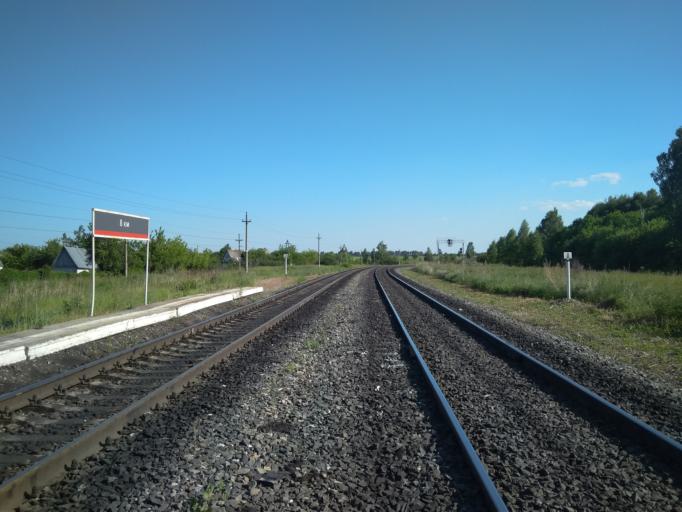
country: RU
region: Ulyanovsk
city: Novoul'yanovsk
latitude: 54.2061
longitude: 48.3095
